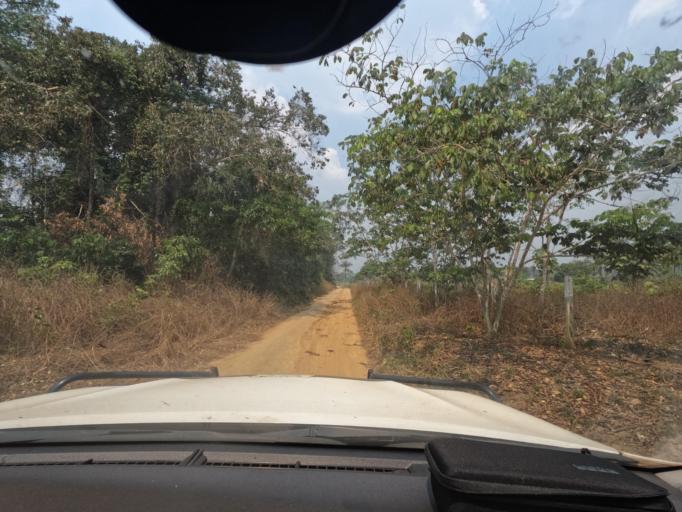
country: BR
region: Rondonia
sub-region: Porto Velho
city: Porto Velho
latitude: -8.7729
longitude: -63.1134
